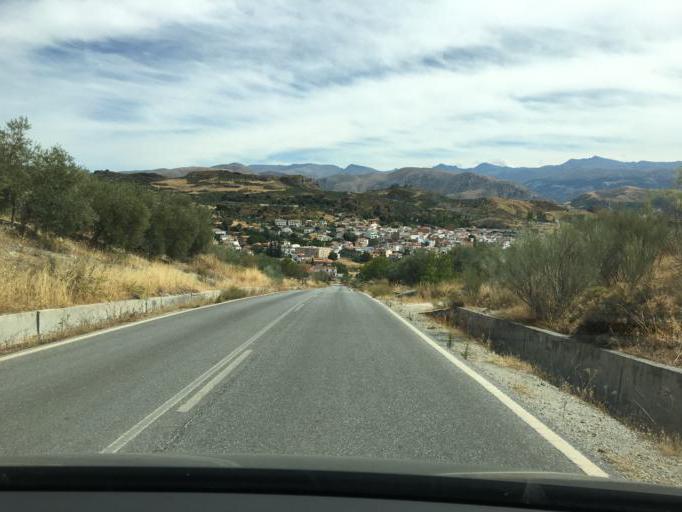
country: ES
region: Andalusia
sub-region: Provincia de Granada
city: Beas de Granada
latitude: 37.2240
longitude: -3.4877
